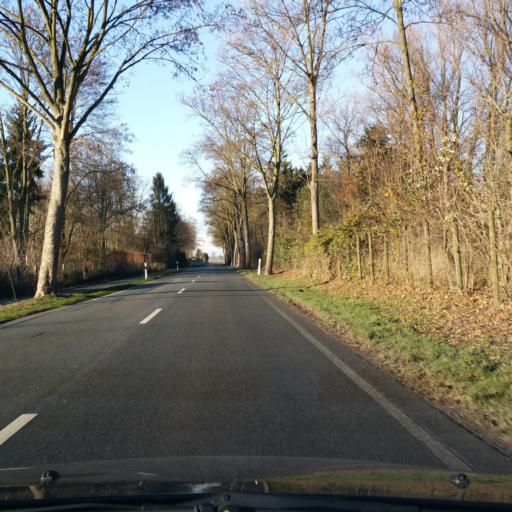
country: DE
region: North Rhine-Westphalia
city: Kalkar
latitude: 51.7342
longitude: 6.3374
